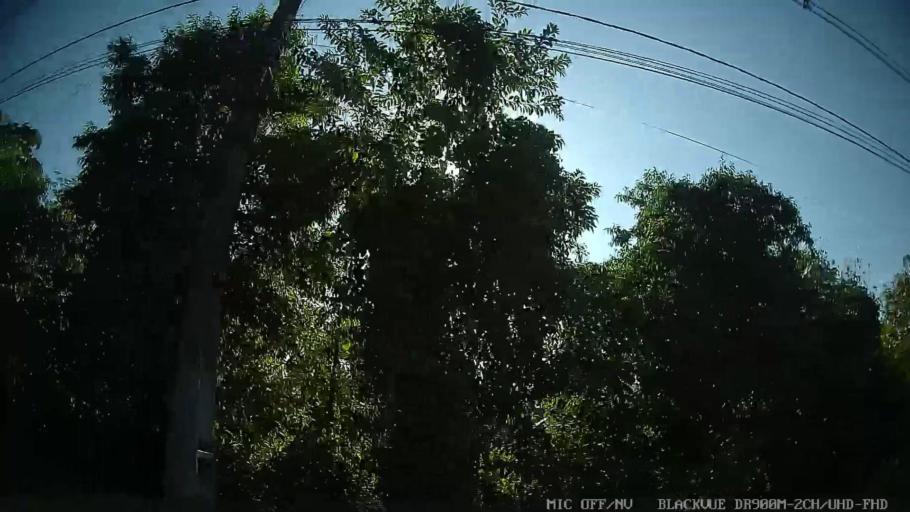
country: BR
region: Sao Paulo
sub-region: Guaruja
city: Guaruja
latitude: -23.9720
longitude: -46.2175
